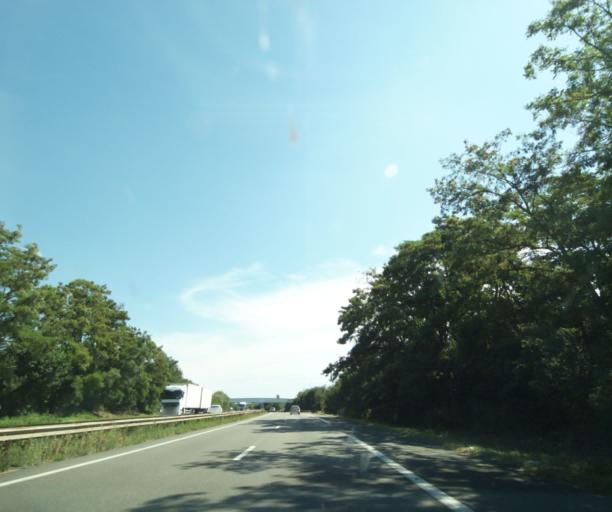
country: FR
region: Lorraine
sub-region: Departement de Meurthe-et-Moselle
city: Dommartin-les-Toul
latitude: 48.6593
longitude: 5.9084
